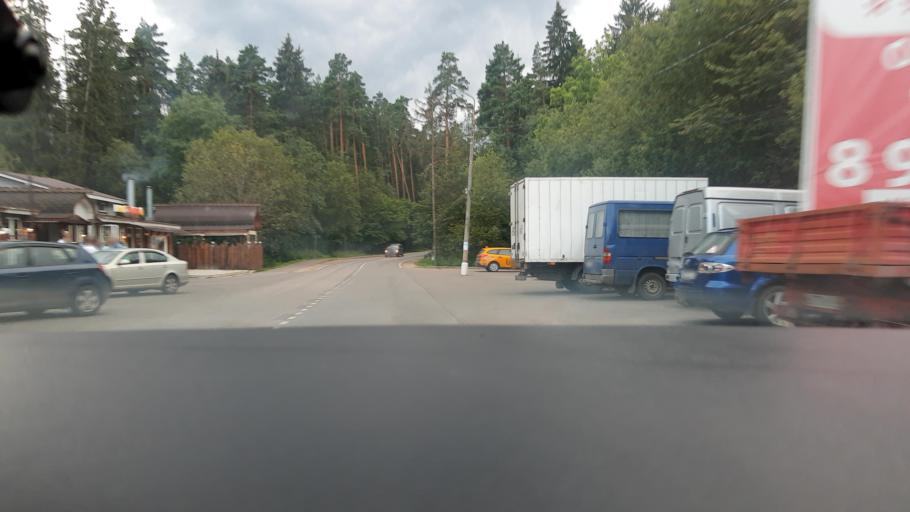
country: RU
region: Moskovskaya
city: Lesnoy Gorodok
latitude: 55.6783
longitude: 37.1879
